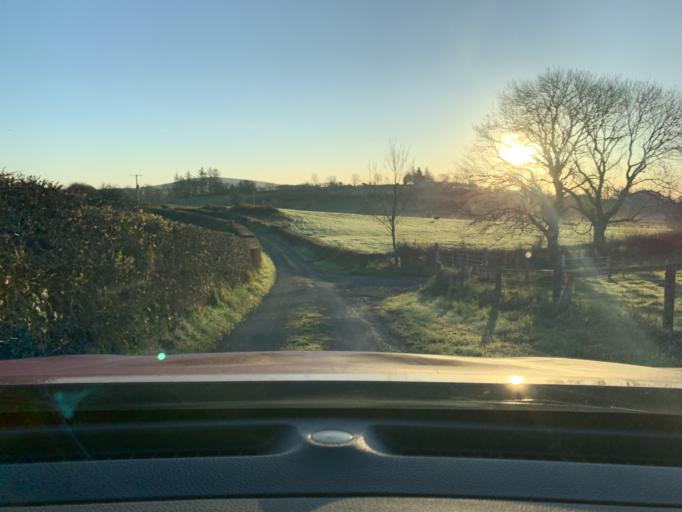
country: IE
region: Connaught
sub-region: Sligo
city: Ballymote
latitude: 54.0674
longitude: -8.5420
